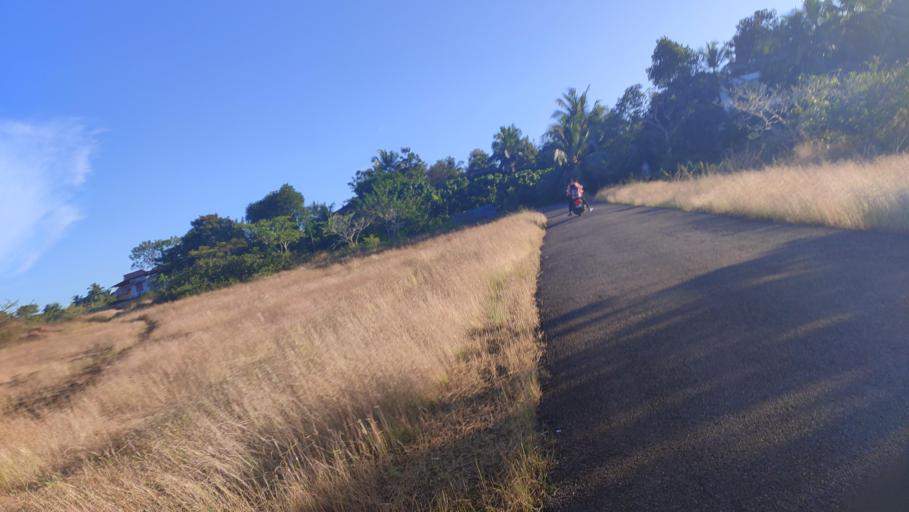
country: IN
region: Kerala
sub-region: Kasaragod District
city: Kasaragod
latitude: 12.5003
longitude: 75.0803
